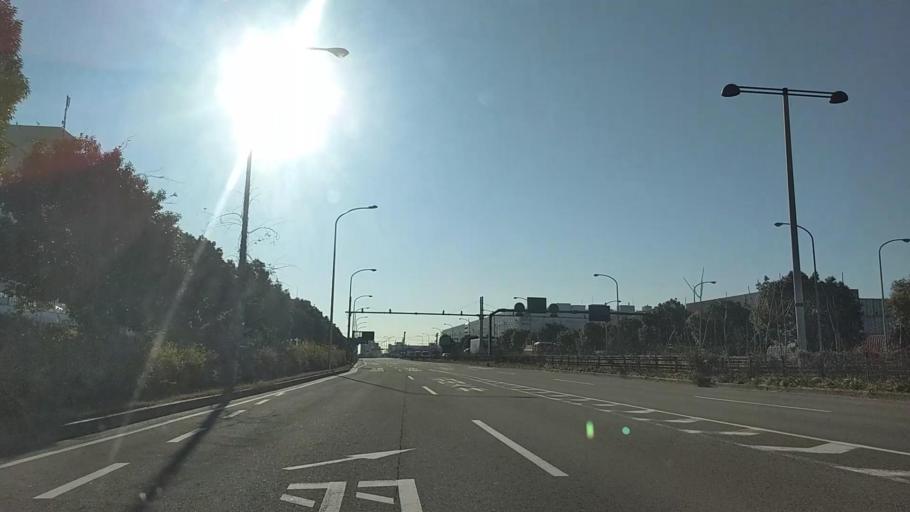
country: JP
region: Kanagawa
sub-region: Kawasaki-shi
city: Kawasaki
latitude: 35.6161
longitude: 139.7831
